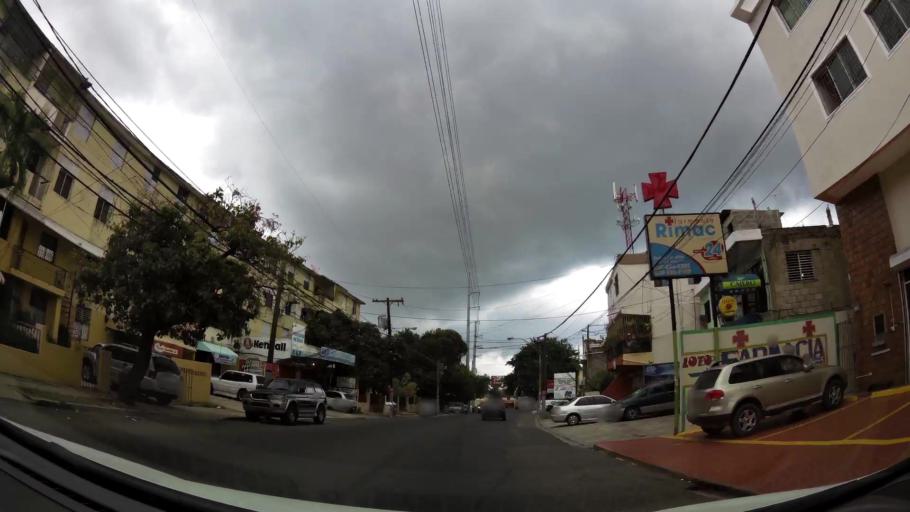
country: DO
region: Nacional
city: La Julia
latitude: 18.4563
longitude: -69.9283
